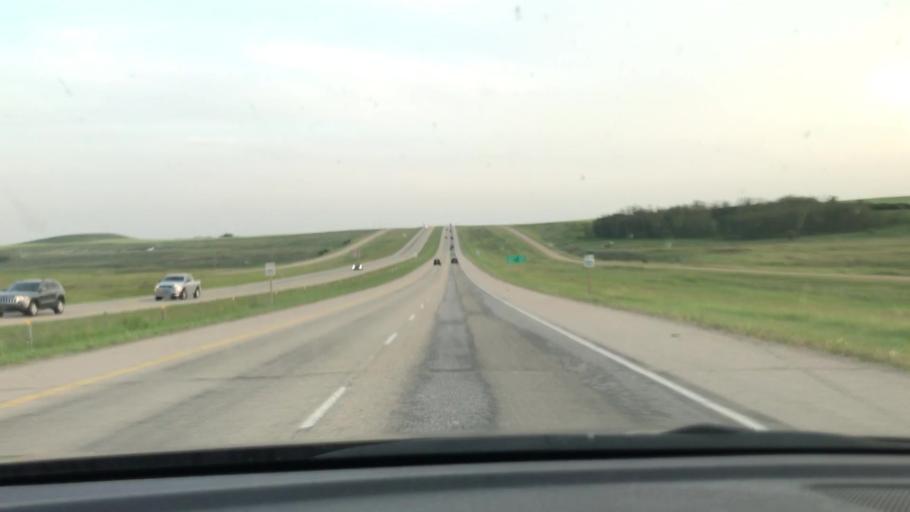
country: CA
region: Alberta
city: Carstairs
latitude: 51.5521
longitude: -114.0253
